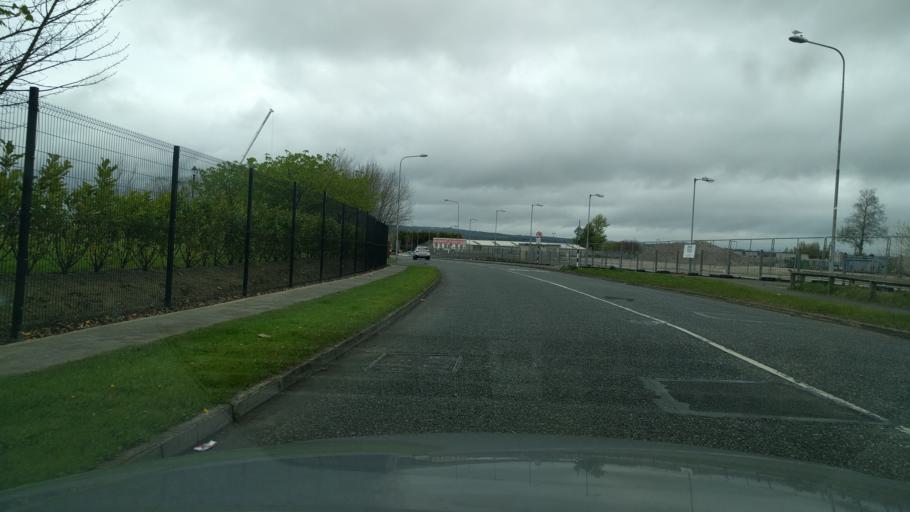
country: IE
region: Leinster
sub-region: Lu
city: Drogheda
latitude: 53.7042
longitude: -6.3692
